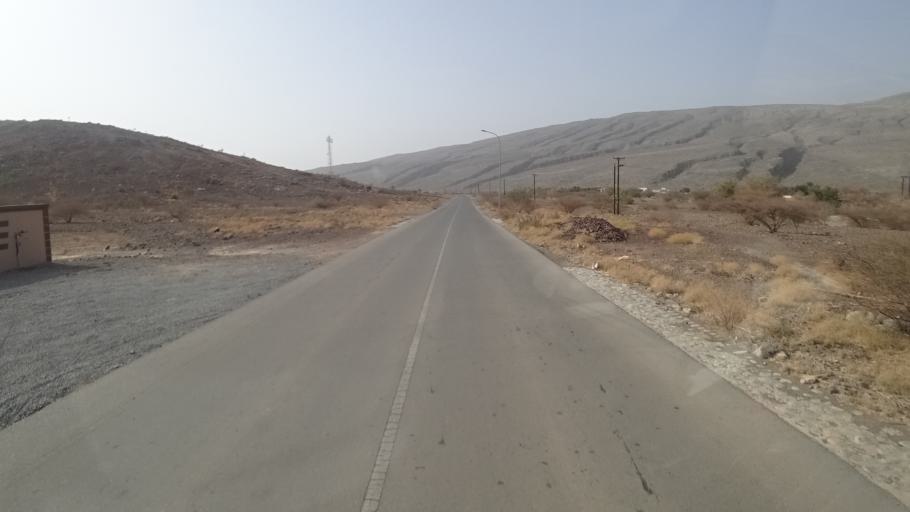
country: OM
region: Muhafazat ad Dakhiliyah
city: Bahla'
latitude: 23.0521
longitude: 57.4213
